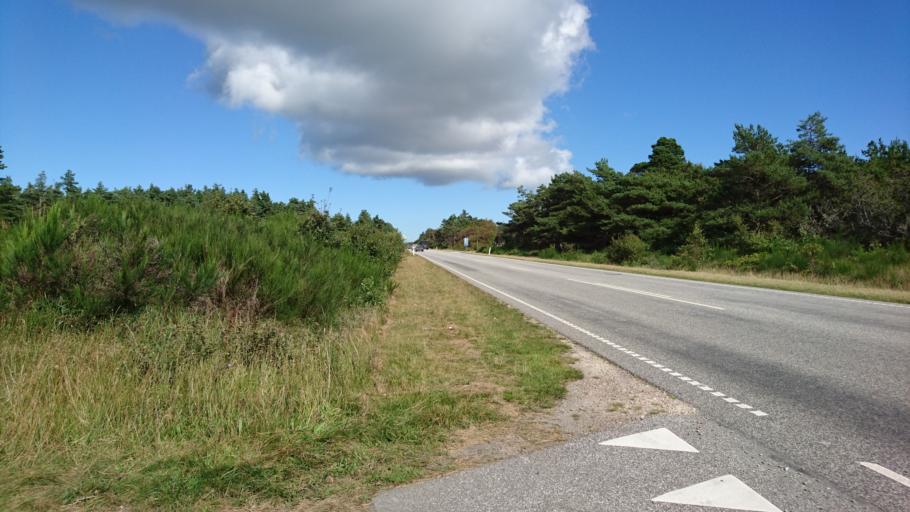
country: DK
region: North Denmark
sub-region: Frederikshavn Kommune
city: Skagen
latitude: 57.7077
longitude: 10.5185
